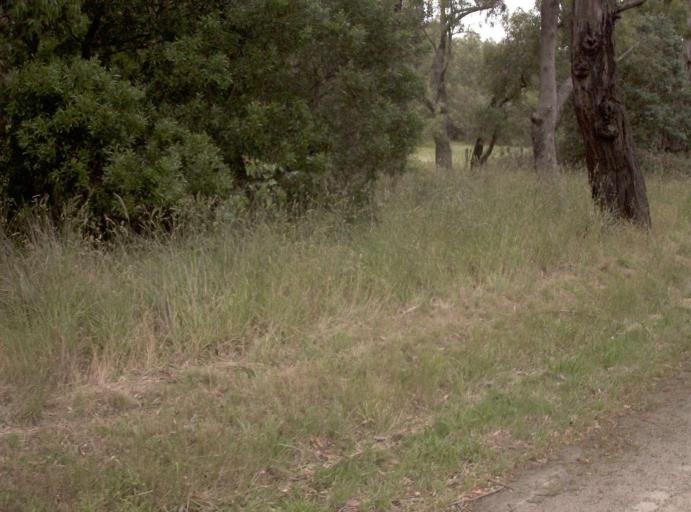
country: AU
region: Victoria
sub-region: Latrobe
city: Traralgon
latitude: -38.2526
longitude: 146.4928
